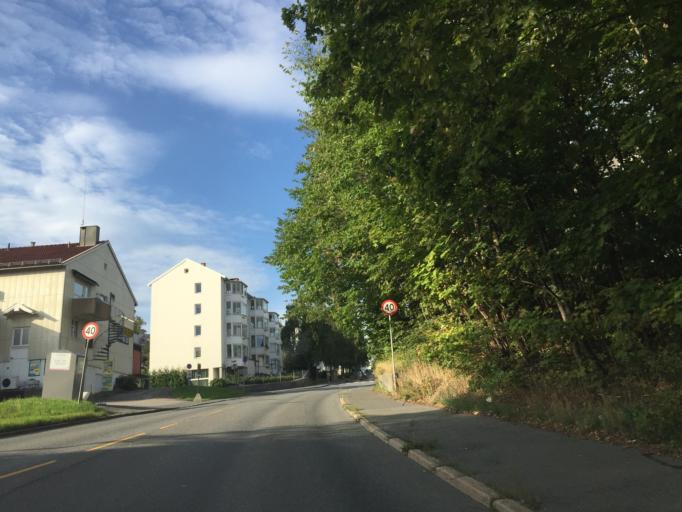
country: NO
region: Akershus
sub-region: Oppegard
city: Kolbotn
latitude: 59.8767
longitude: 10.8186
